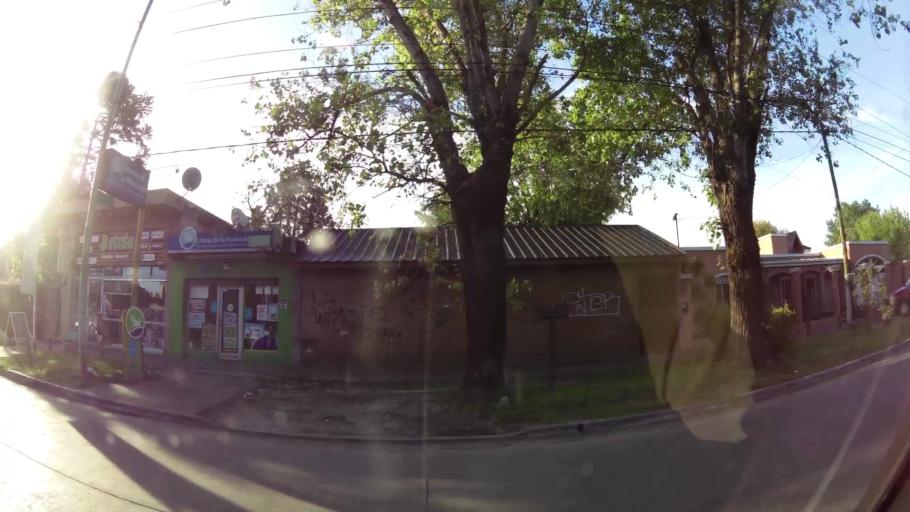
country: AR
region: Buenos Aires
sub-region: Partido de Quilmes
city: Quilmes
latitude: -34.7860
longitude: -58.2104
